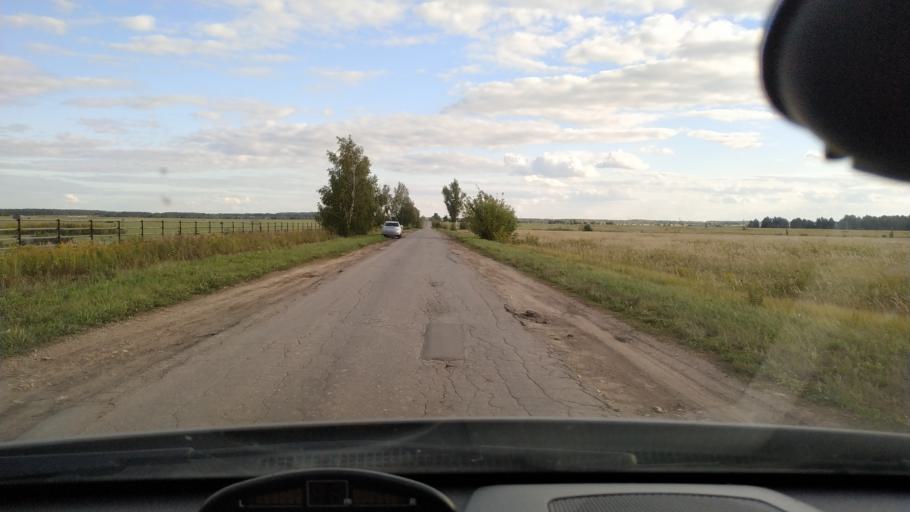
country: RU
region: Rjazan
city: Polyany
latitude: 54.5764
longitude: 39.8609
